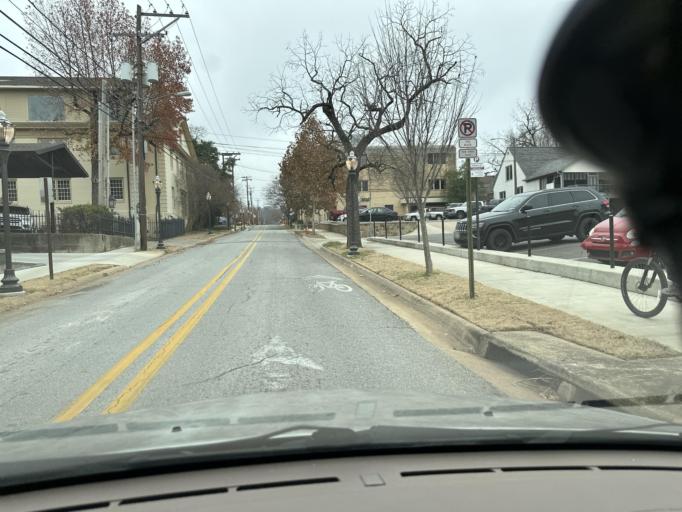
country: US
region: Arkansas
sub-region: Washington County
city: Fayetteville
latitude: 36.0647
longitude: -94.1604
